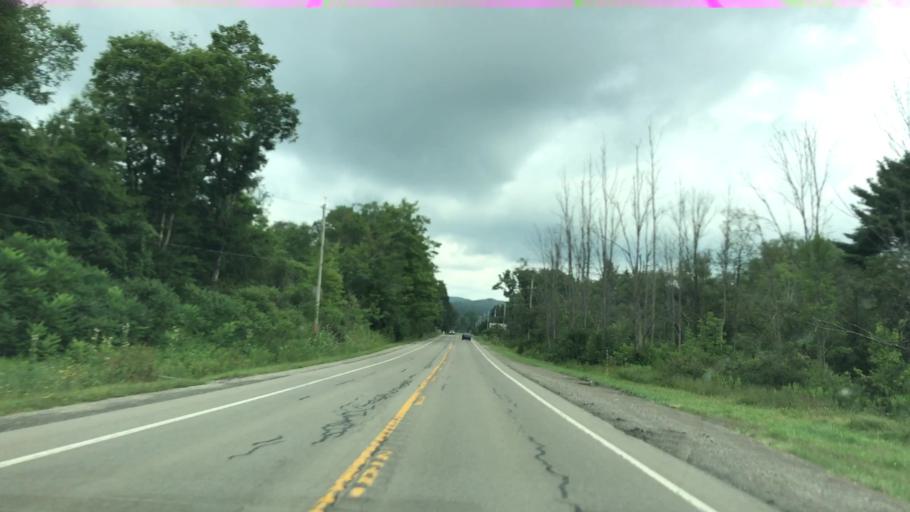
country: US
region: New York
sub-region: Steuben County
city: Bath
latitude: 42.3945
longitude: -77.3481
